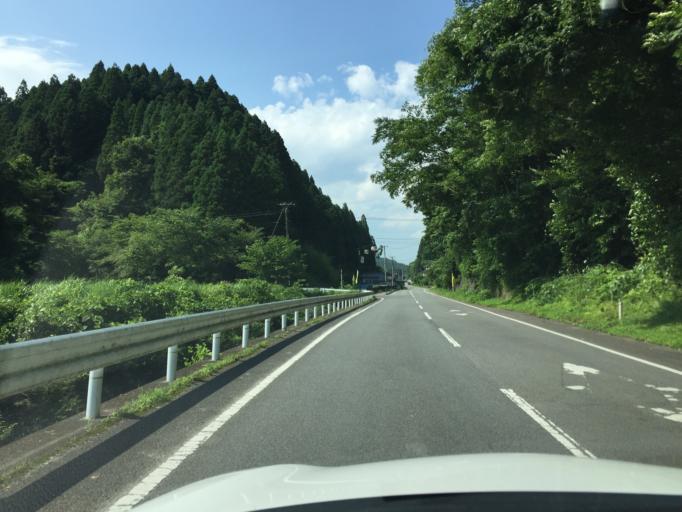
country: JP
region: Ibaraki
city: Kitaibaraki
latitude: 36.9546
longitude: 140.7044
